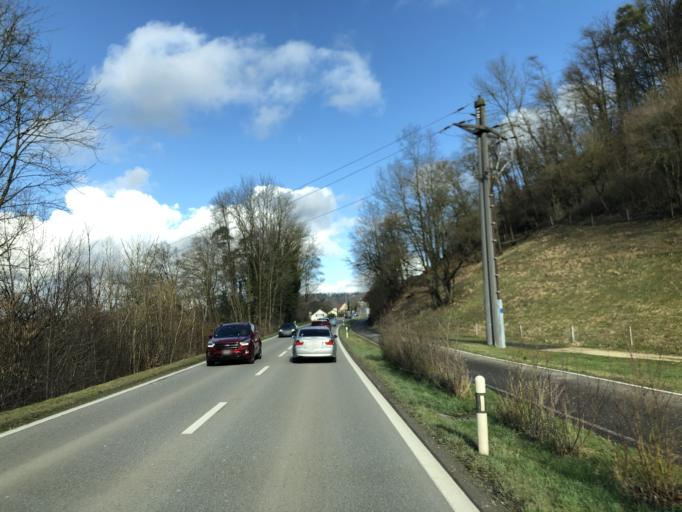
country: CH
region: Aargau
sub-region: Bezirk Baden
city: Gebenstorf
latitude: 47.4727
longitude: 8.2335
